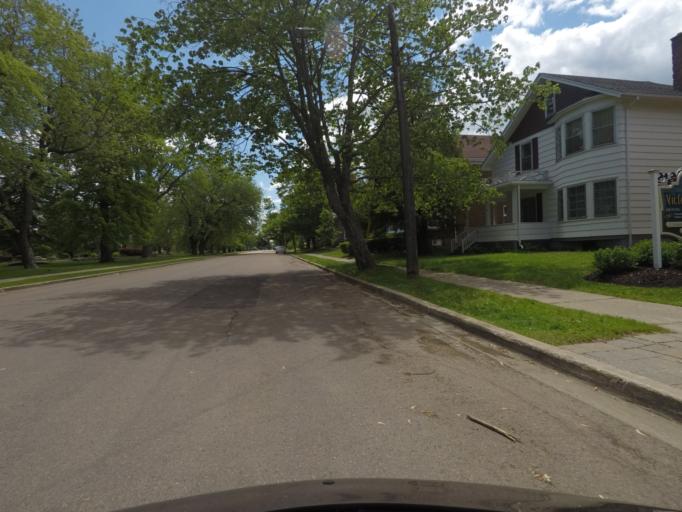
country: CA
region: New Brunswick
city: Moncton
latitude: 46.0935
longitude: -64.7909
